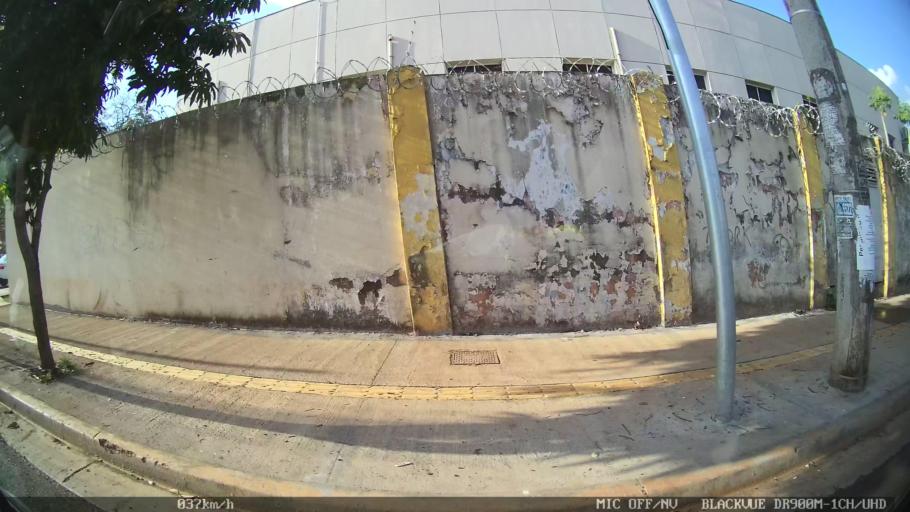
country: BR
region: Sao Paulo
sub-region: Ribeirao Preto
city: Ribeirao Preto
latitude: -21.1589
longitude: -47.8155
